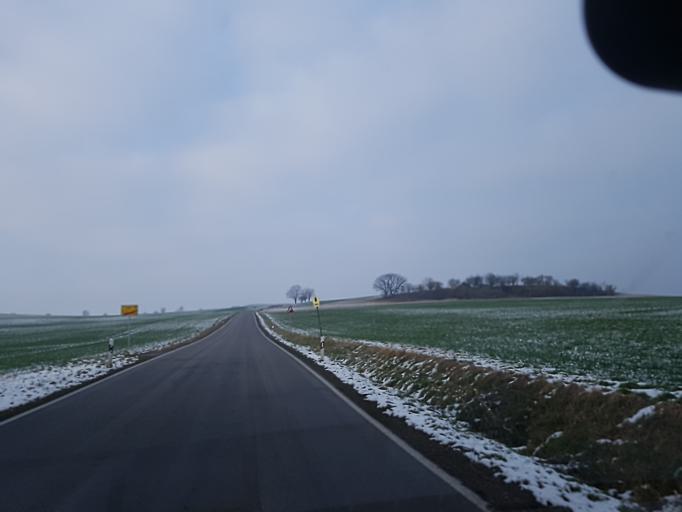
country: DE
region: Saxony
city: Cavertitz
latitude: 51.3490
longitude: 13.1393
